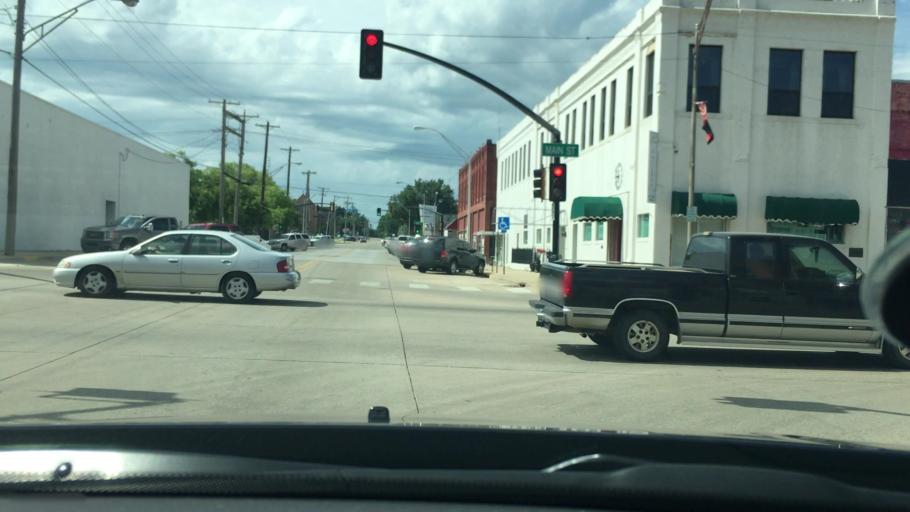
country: US
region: Oklahoma
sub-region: Pontotoc County
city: Ada
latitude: 34.7747
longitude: -96.6803
